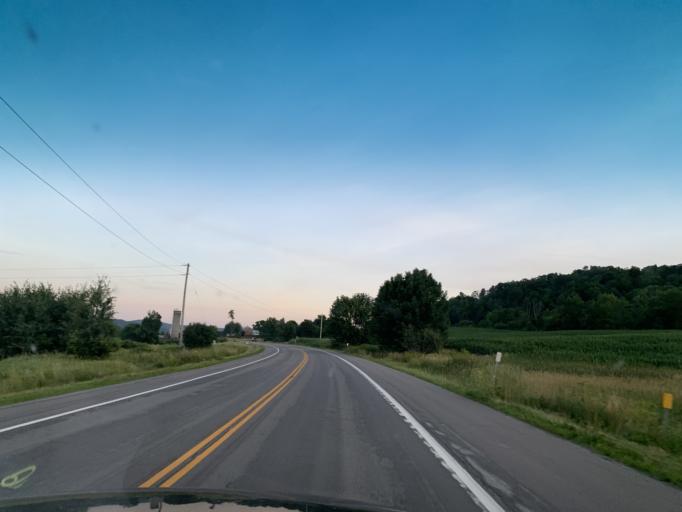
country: US
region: New York
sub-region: Oneida County
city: Waterville
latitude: 42.8567
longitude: -75.2528
